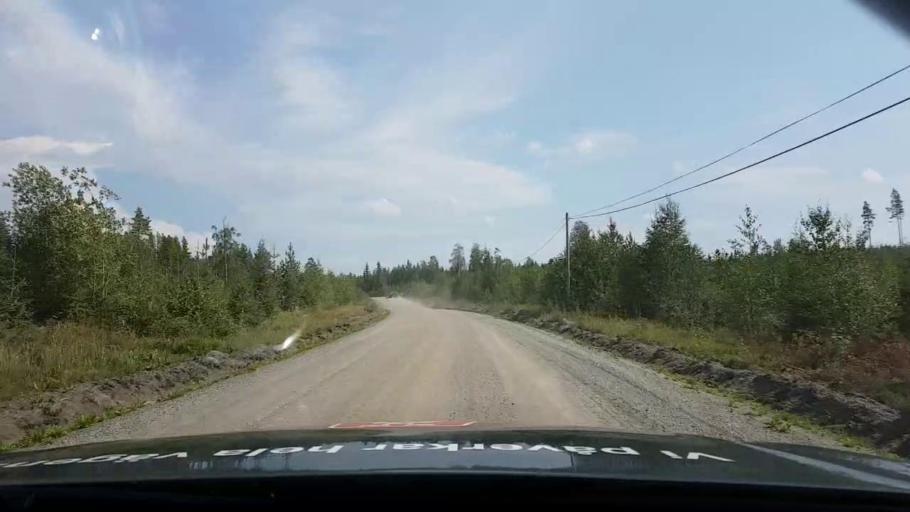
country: SE
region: Jaemtland
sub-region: Braecke Kommun
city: Braecke
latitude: 62.7403
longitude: 15.4386
